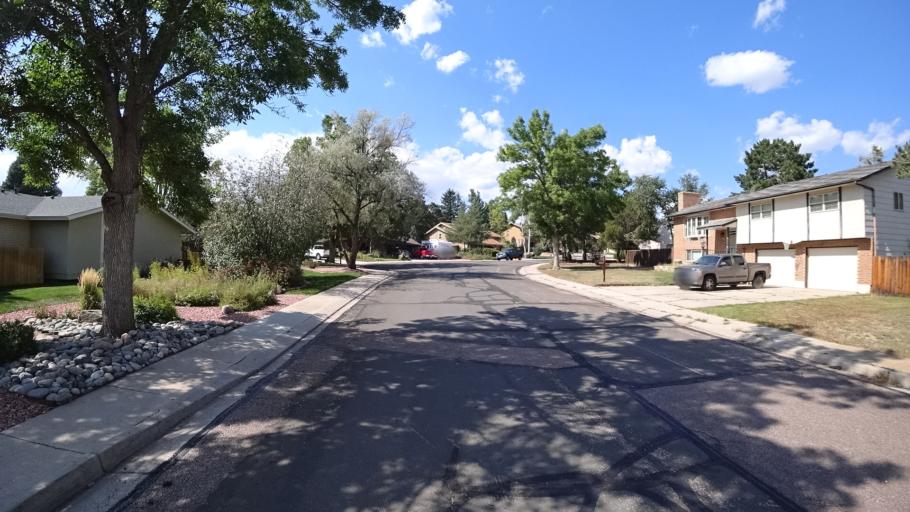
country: US
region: Colorado
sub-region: El Paso County
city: Cimarron Hills
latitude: 38.8760
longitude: -104.7506
